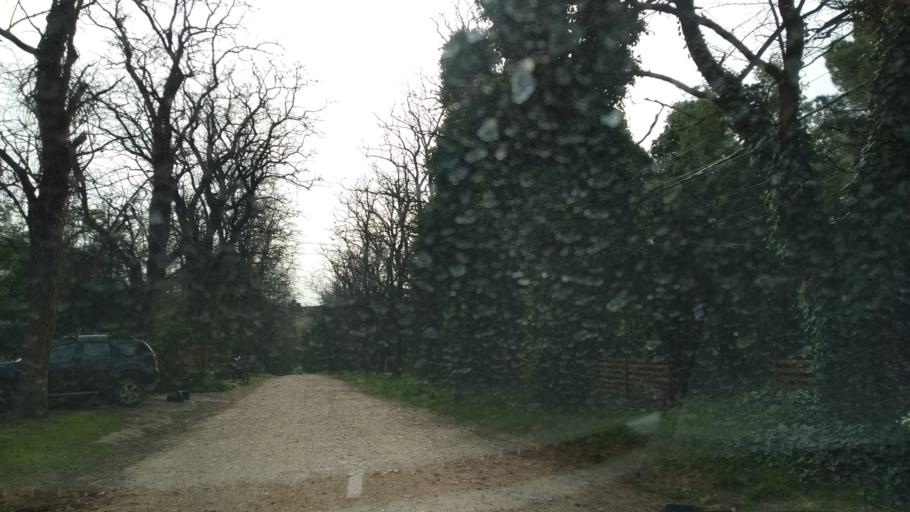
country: AR
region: Buenos Aires
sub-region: Partido de Tornquist
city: Tornquist
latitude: -38.0825
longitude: -61.9368
